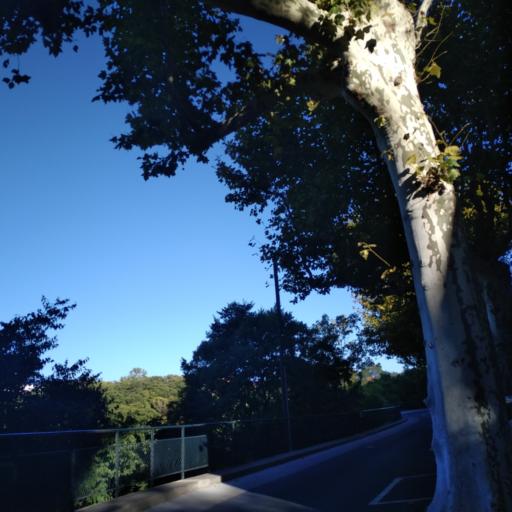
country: FR
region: Languedoc-Roussillon
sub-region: Departement des Pyrenees-Orientales
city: la Roca d'Albera
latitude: 42.5205
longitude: 2.9326
